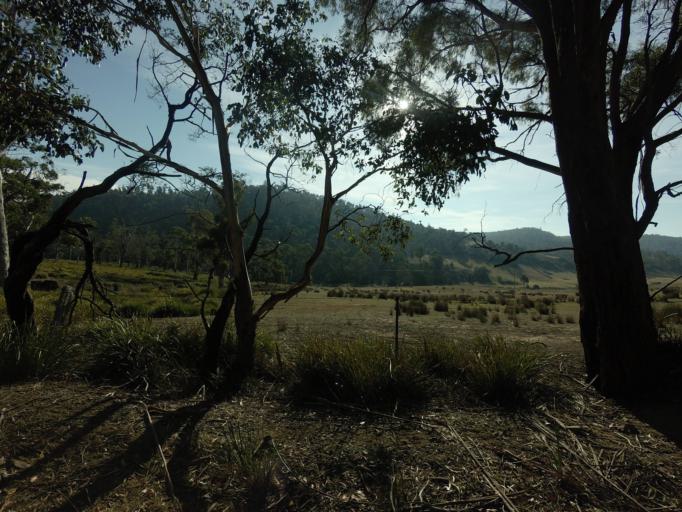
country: AU
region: Tasmania
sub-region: Sorell
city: Sorell
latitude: -42.5360
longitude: 147.4349
